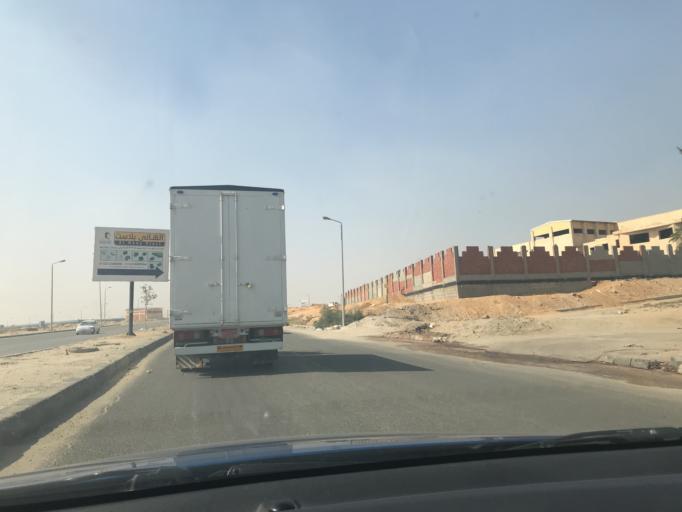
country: EG
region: Eastern Province
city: Bilbays
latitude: 30.2548
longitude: 31.7575
